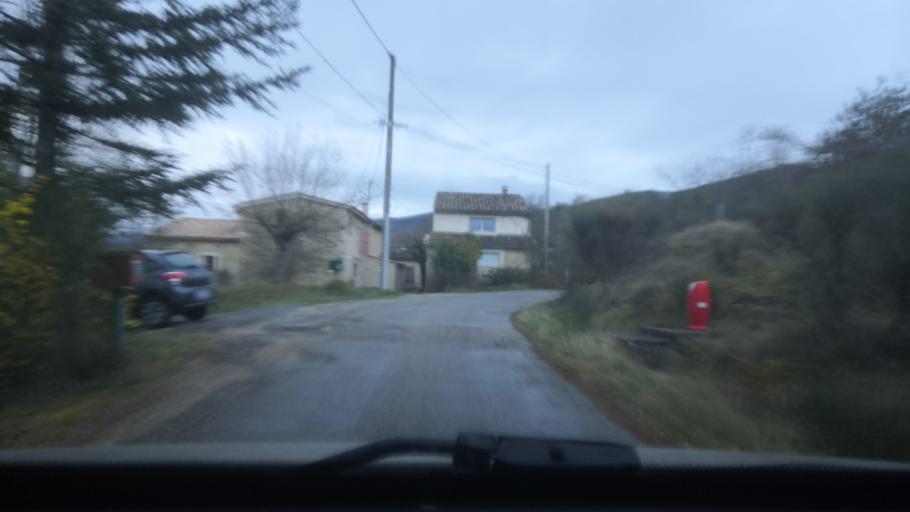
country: FR
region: Rhone-Alpes
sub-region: Departement de la Drome
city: Dieulefit
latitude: 44.5188
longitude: 5.0297
